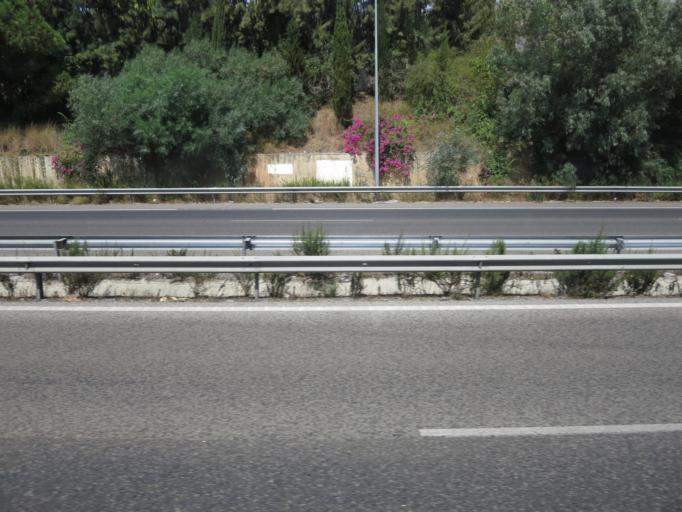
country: ES
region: Andalusia
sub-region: Provincia de Malaga
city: Marbella
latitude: 36.5154
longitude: -4.9098
